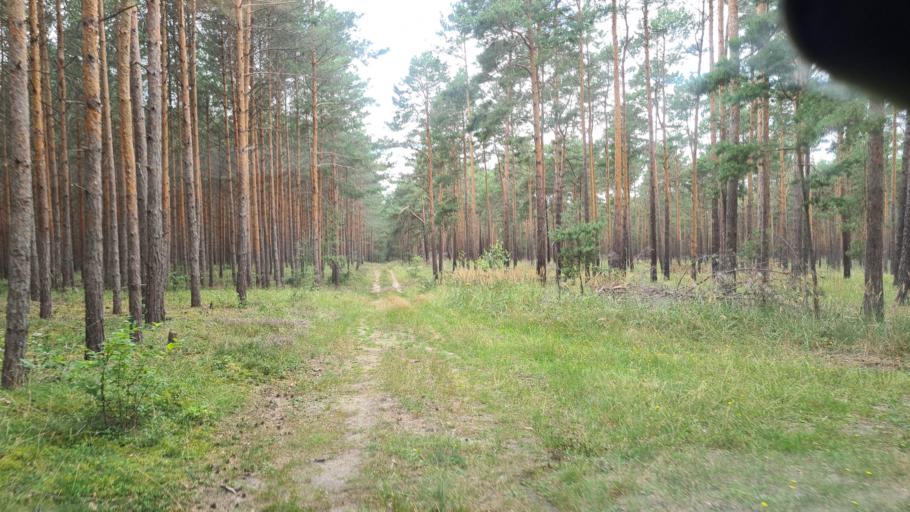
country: DE
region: Brandenburg
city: Sallgast
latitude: 51.5847
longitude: 13.8956
